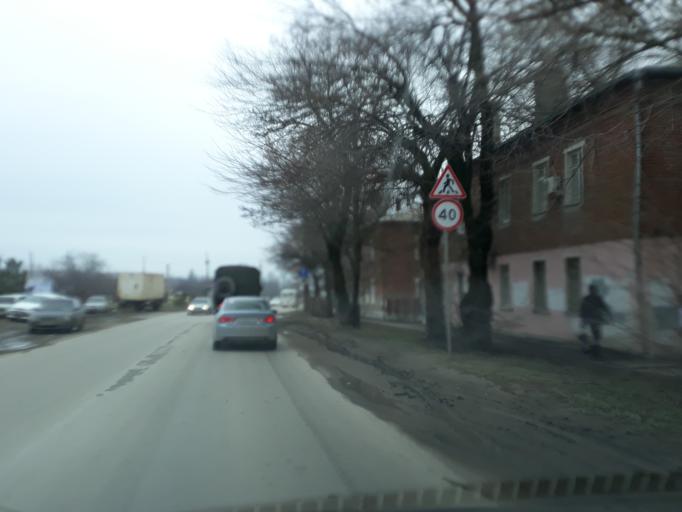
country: RU
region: Rostov
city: Taganrog
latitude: 47.2173
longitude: 38.8823
